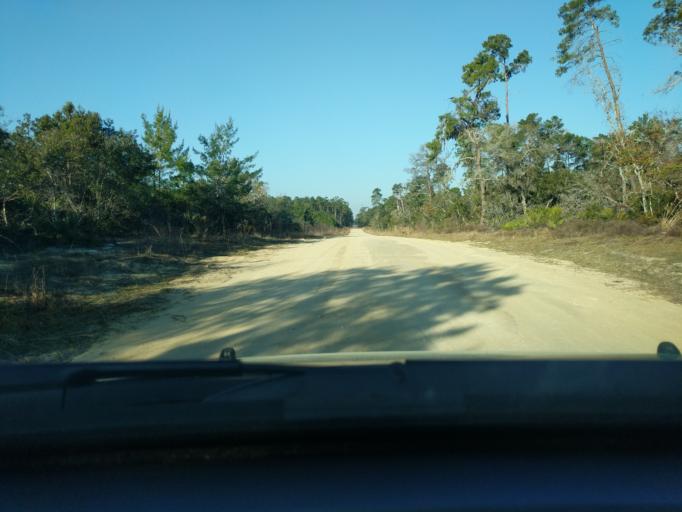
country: US
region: Florida
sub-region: Marion County
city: Silver Springs Shores
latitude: 29.2264
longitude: -81.8104
